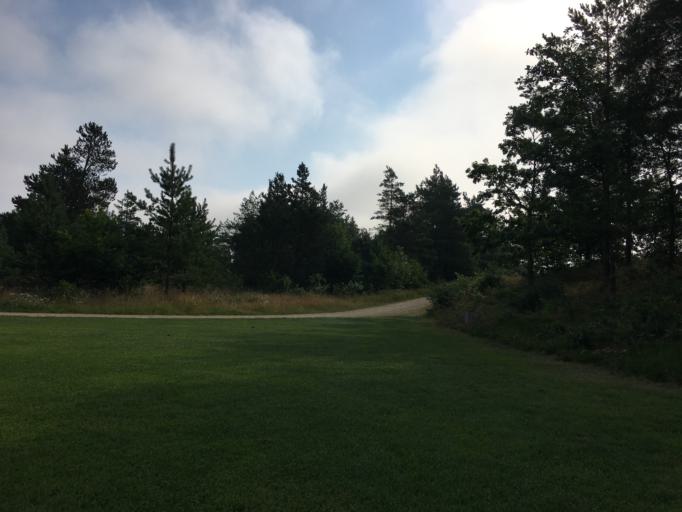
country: DK
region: Central Jutland
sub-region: Holstebro Kommune
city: Ulfborg
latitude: 56.3235
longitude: 8.4197
